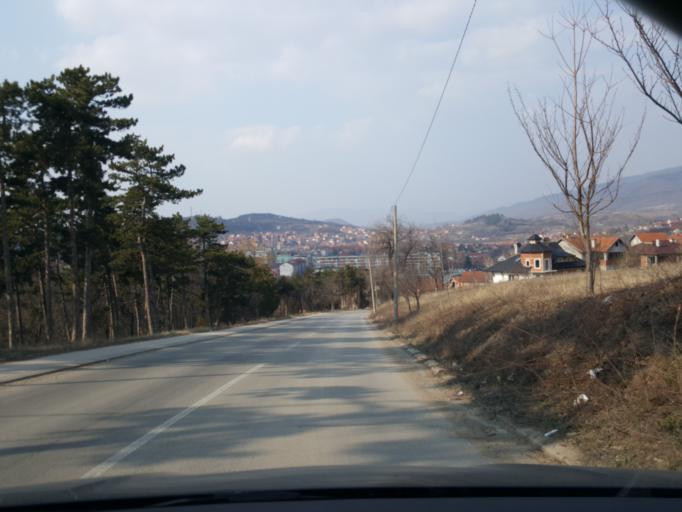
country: RS
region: Central Serbia
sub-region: Nisavski Okrug
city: Aleksinac
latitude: 43.5341
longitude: 21.7134
